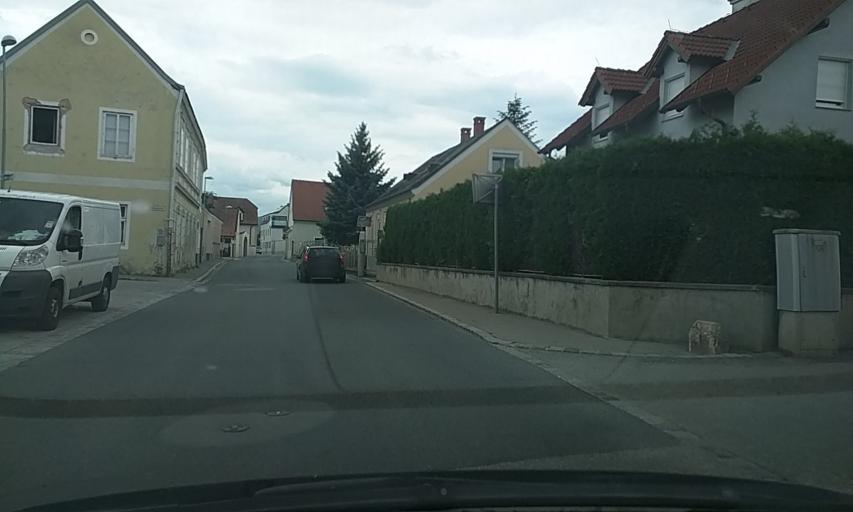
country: AT
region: Lower Austria
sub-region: Politischer Bezirk Krems
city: Weinzierl bei Krems
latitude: 48.3848
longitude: 15.6127
